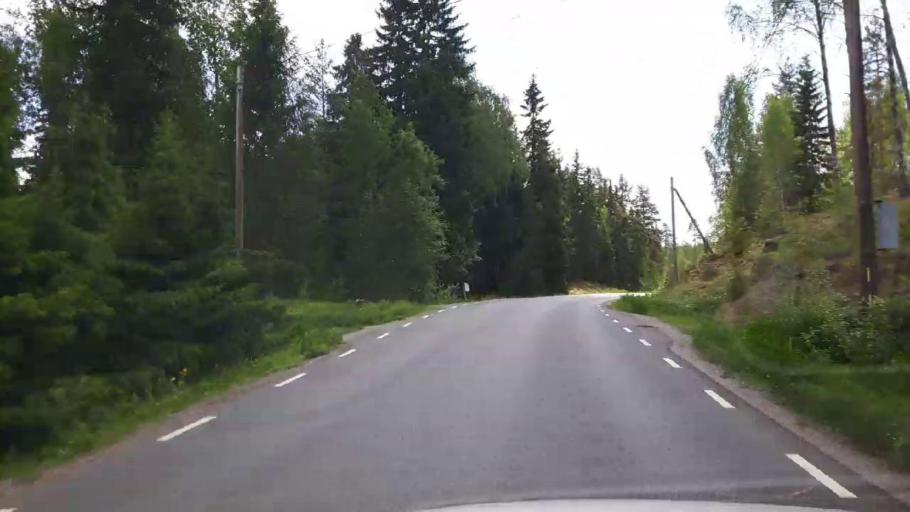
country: SE
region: Dalarna
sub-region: Faluns Kommun
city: Falun
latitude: 60.6621
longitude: 15.7618
